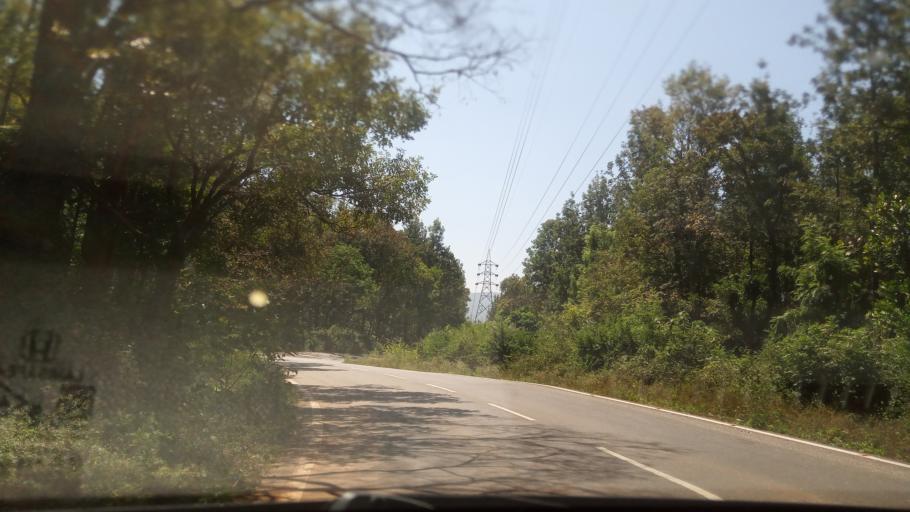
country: IN
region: Karnataka
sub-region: Chikmagalur
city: Chikmagalur
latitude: 13.4506
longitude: 75.8018
